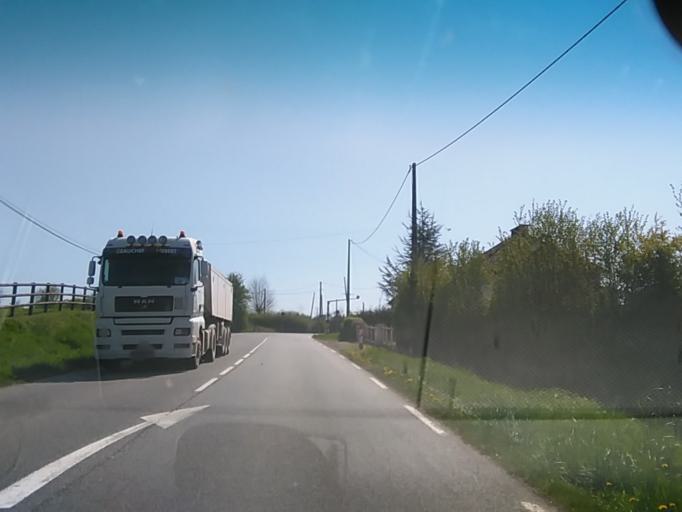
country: FR
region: Lower Normandy
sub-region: Departement de l'Orne
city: Gace
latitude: 48.7052
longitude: 0.2263
